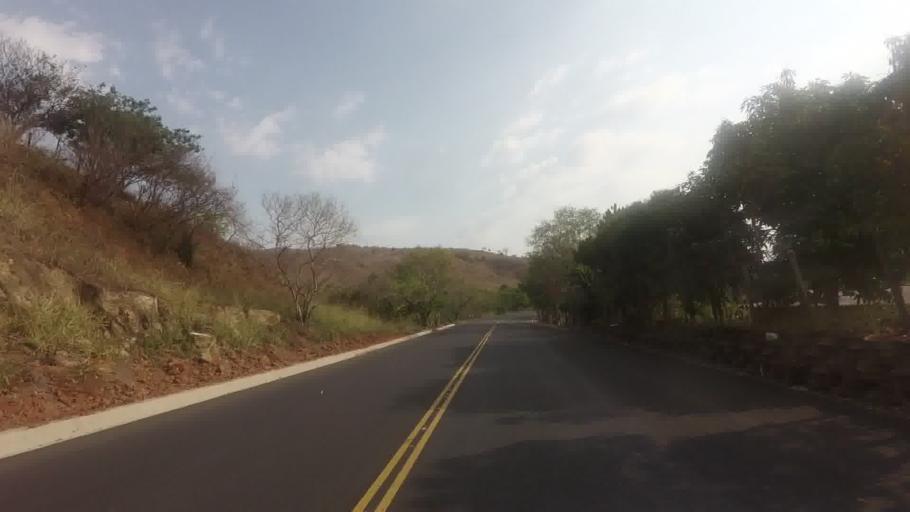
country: BR
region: Rio de Janeiro
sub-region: Itaperuna
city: Itaperuna
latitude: -21.3101
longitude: -41.8565
